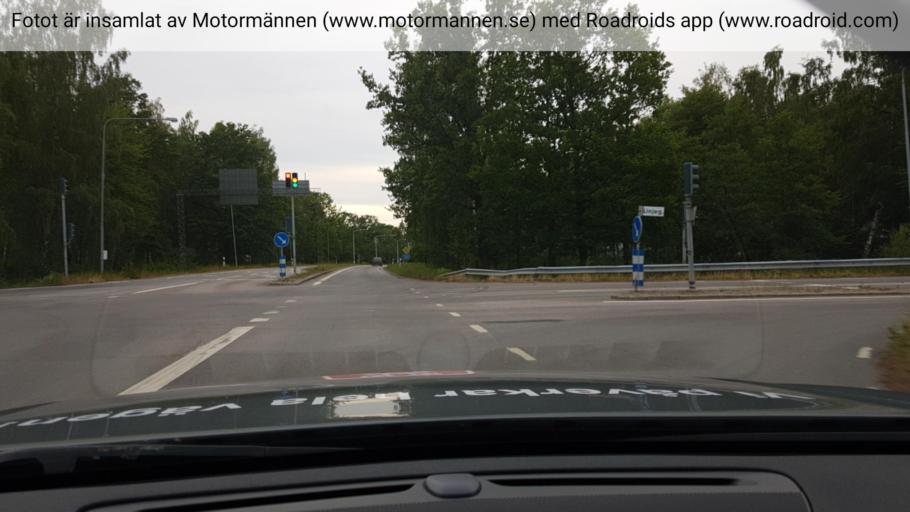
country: SE
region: OEstergoetland
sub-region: Motala Kommun
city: Motala
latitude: 58.5558
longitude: 15.0630
